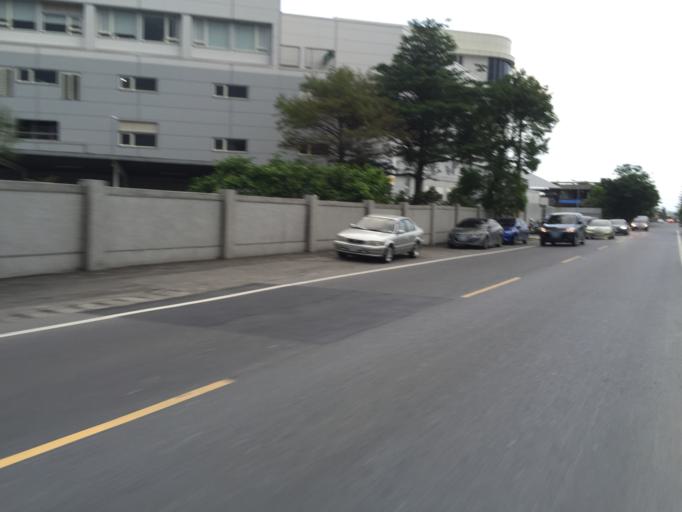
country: TW
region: Taiwan
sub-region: Yilan
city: Yilan
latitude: 24.7807
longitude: 121.7338
